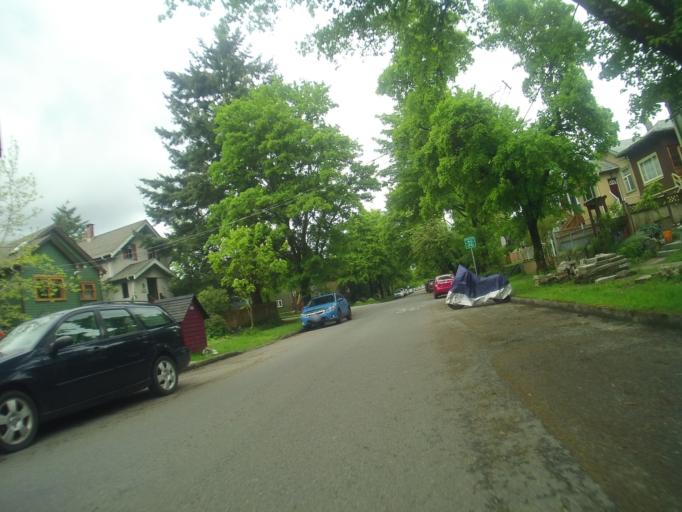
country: CA
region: British Columbia
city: Vancouver
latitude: 49.2428
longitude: -123.0975
